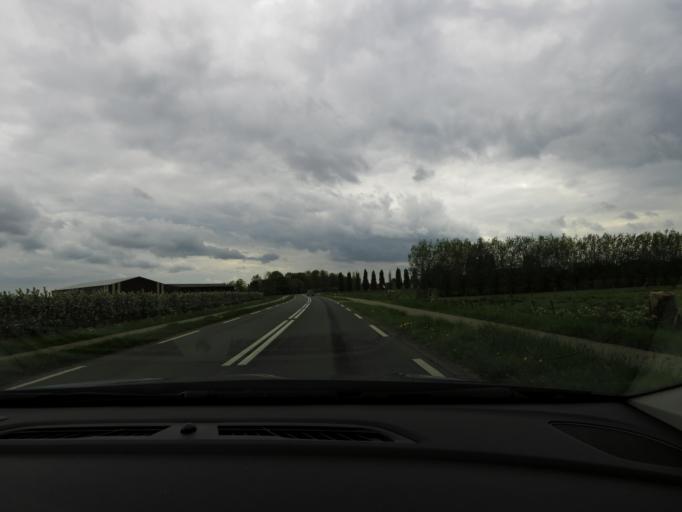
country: NL
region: Gelderland
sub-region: Gemeente Maasdriel
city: Heerewaarden
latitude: 51.8390
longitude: 5.4301
